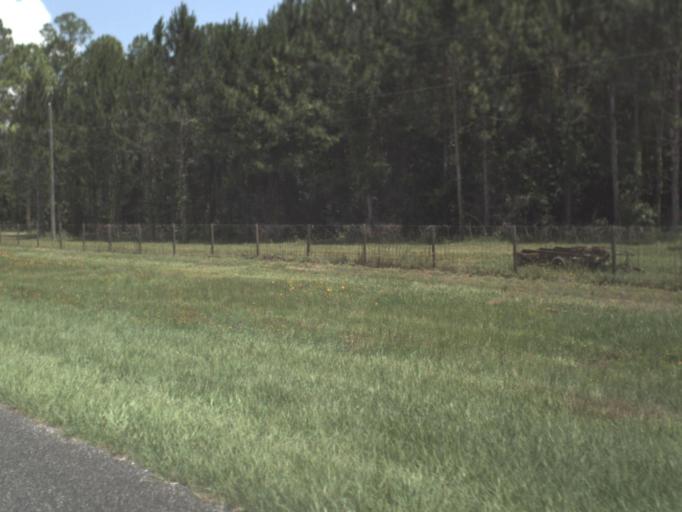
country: US
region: Florida
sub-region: Alachua County
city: High Springs
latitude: 29.8175
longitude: -82.5748
